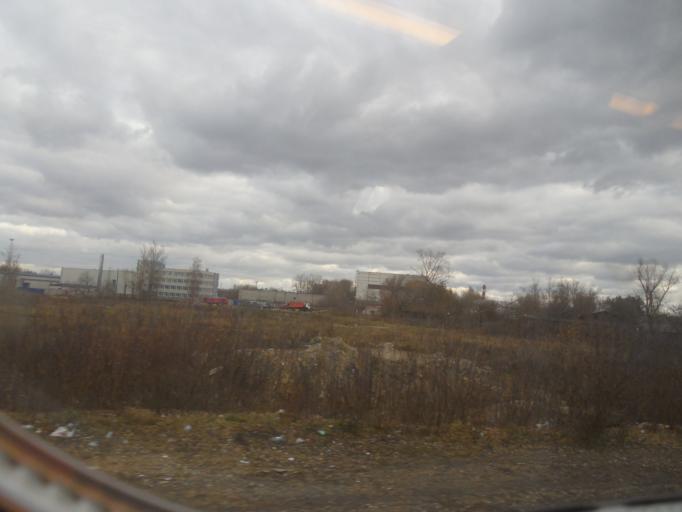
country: RU
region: Moscow
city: Nekrasovka
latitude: 55.6715
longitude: 37.9216
